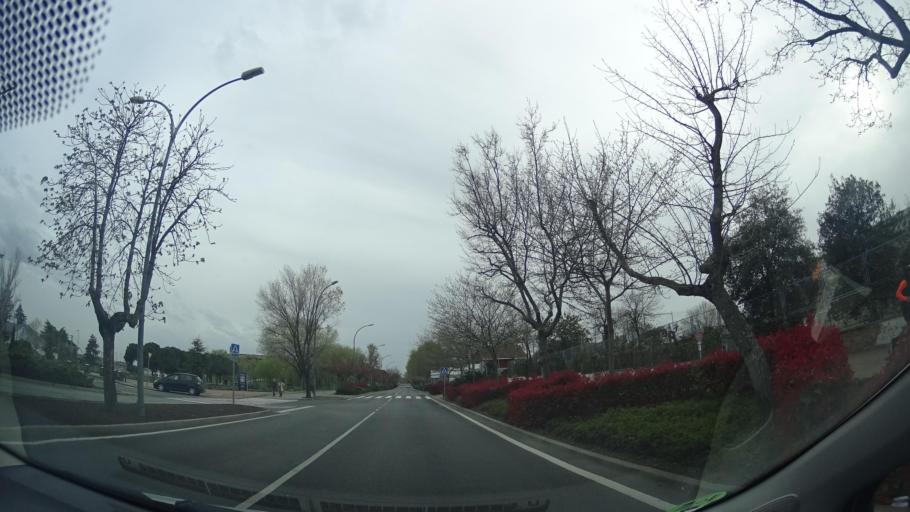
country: ES
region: Madrid
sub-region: Provincia de Madrid
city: Colmenar Viejo
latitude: 40.6698
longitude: -3.7698
